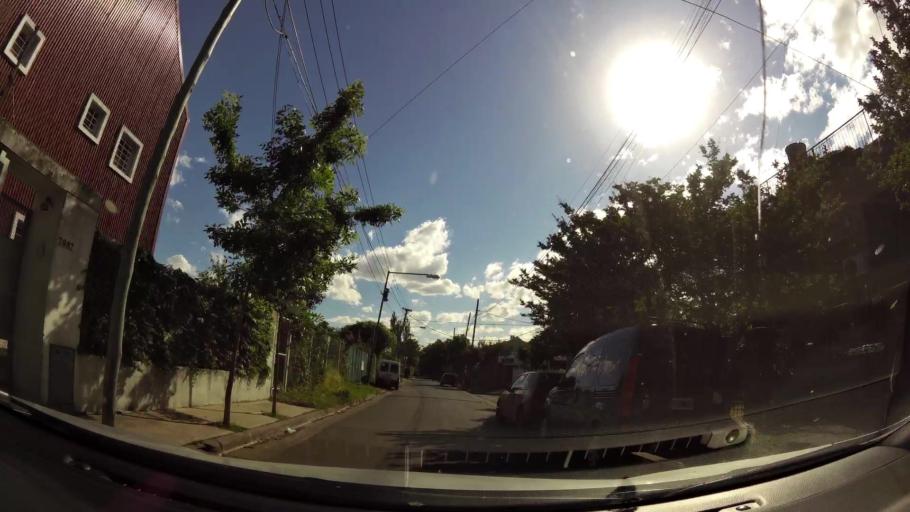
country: AR
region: Buenos Aires
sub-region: Partido de Tigre
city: Tigre
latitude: -34.4731
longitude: -58.5605
